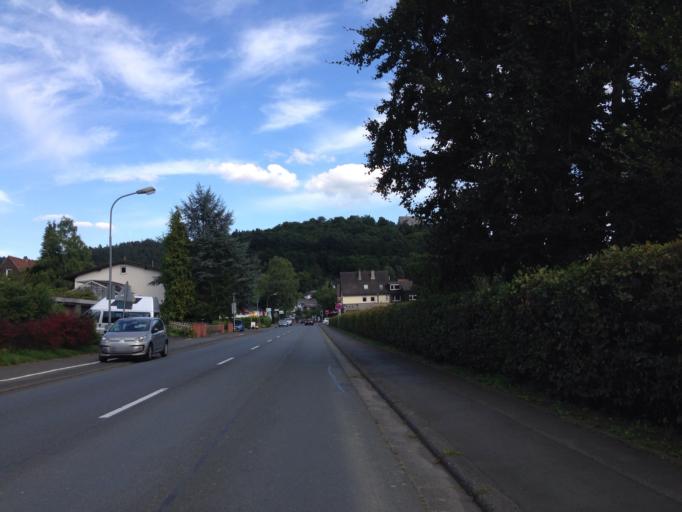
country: DE
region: Hesse
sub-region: Regierungsbezirk Giessen
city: Biedenkopf
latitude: 50.9170
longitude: 8.5165
